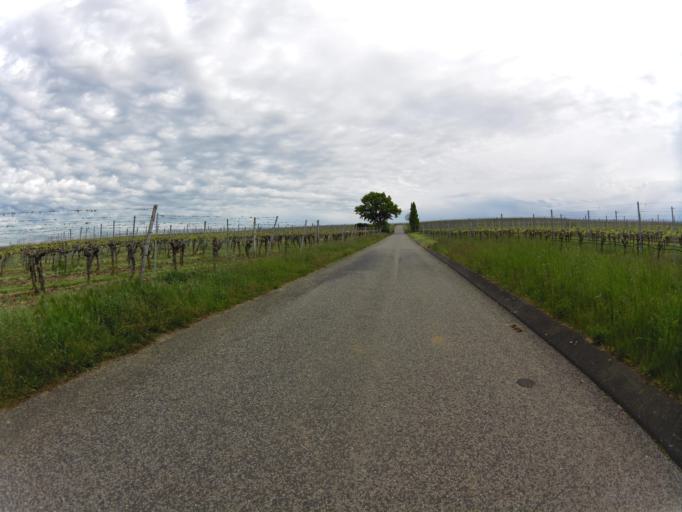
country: DE
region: Bavaria
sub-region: Regierungsbezirk Unterfranken
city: Nordheim
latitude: 49.8539
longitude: 10.1842
